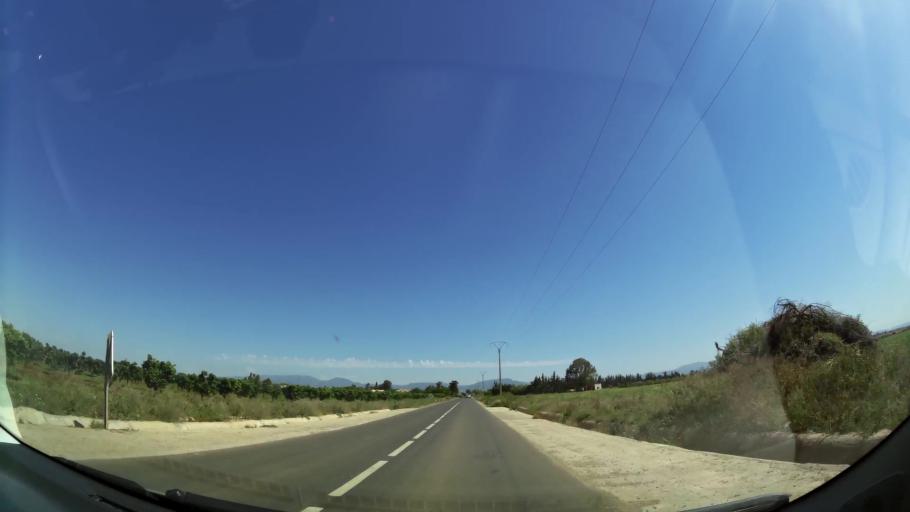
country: MA
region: Oriental
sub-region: Berkane-Taourirt
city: Madagh
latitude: 35.0219
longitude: -2.4090
